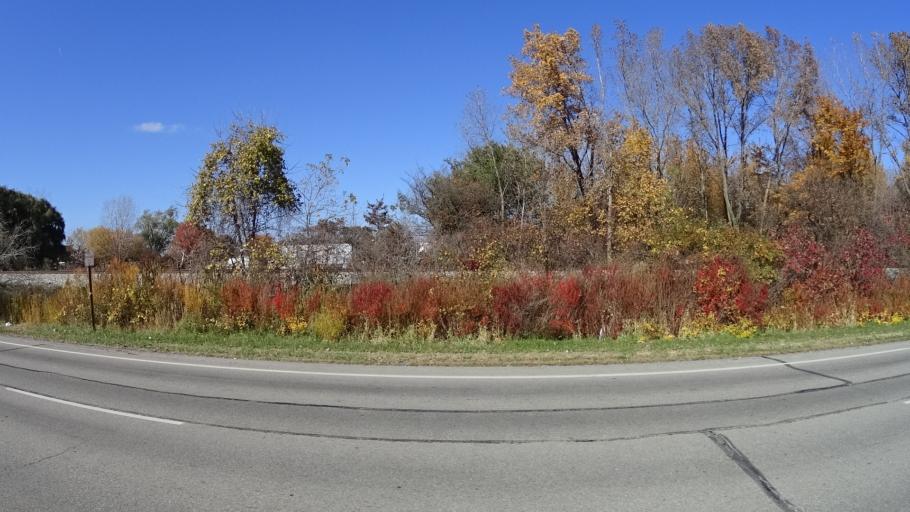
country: US
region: Ohio
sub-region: Lorain County
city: Lorain
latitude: 41.4493
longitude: -82.2150
